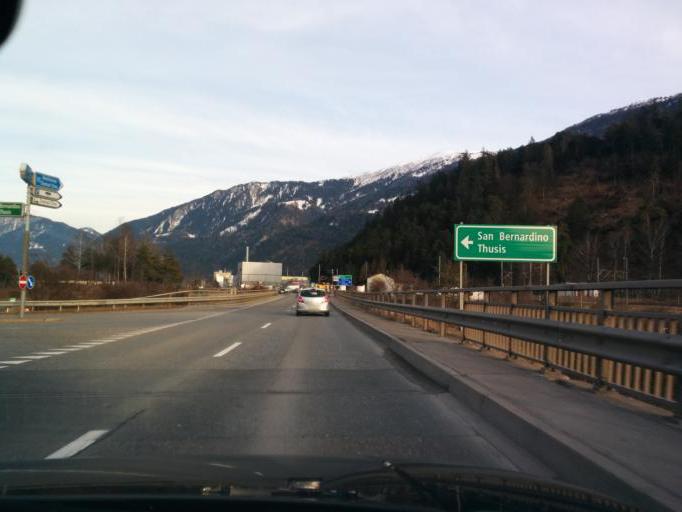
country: CH
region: Grisons
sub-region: Imboden District
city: Tamins
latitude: 46.8284
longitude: 9.4162
